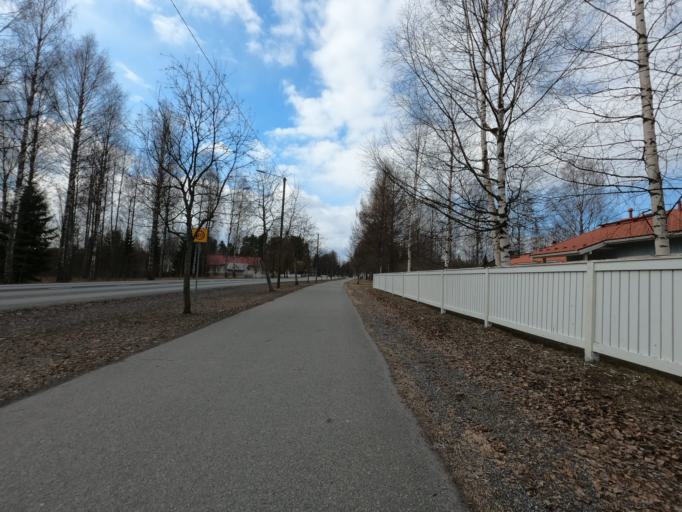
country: FI
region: North Karelia
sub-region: Joensuu
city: Joensuu
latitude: 62.6194
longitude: 29.8620
